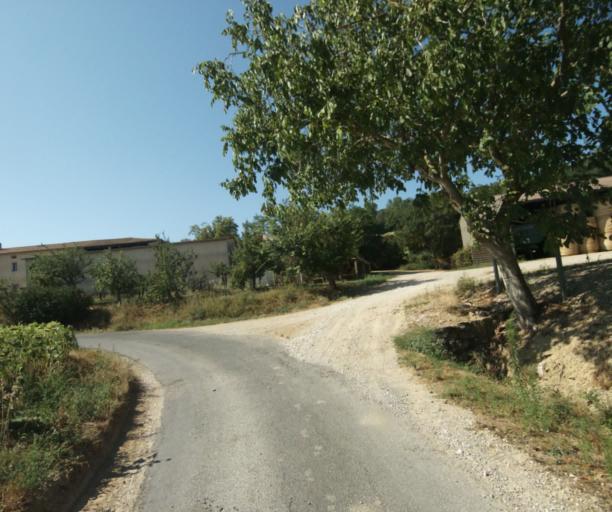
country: FR
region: Midi-Pyrenees
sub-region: Departement de la Haute-Garonne
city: Saint-Felix-Lauragais
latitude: 43.5154
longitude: 1.9350
